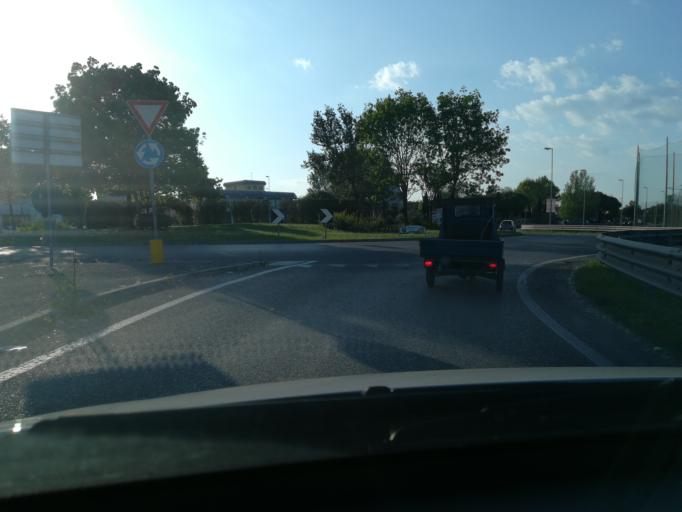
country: IT
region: Emilia-Romagna
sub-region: Provincia di Rimini
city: Riccione
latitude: 44.0024
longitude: 12.6350
